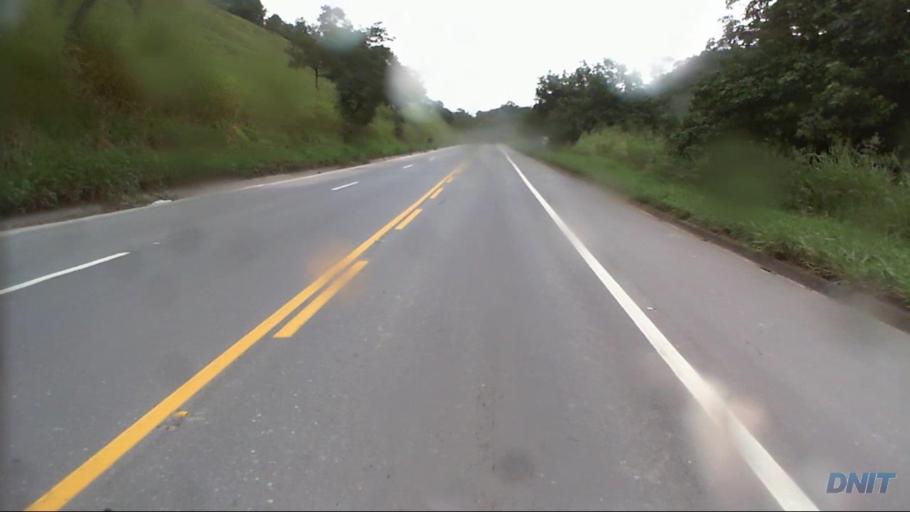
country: BR
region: Minas Gerais
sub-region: Nova Era
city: Nova Era
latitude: -19.7060
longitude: -42.9989
